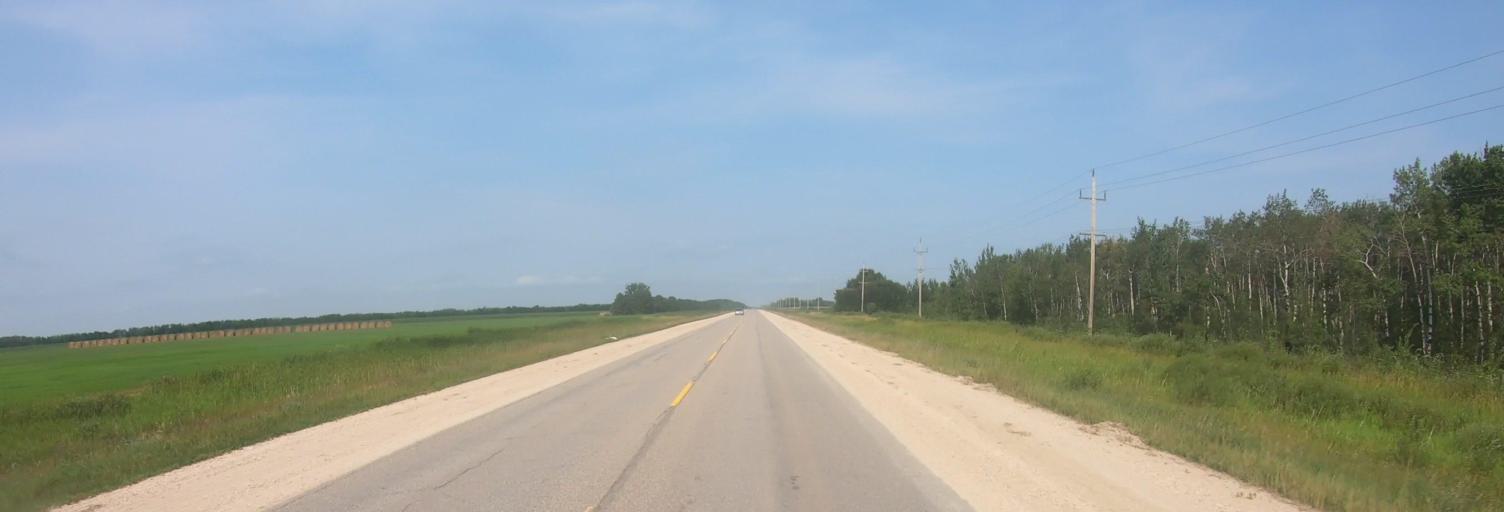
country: CA
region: Manitoba
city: La Broquerie
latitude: 49.3191
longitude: -96.5845
